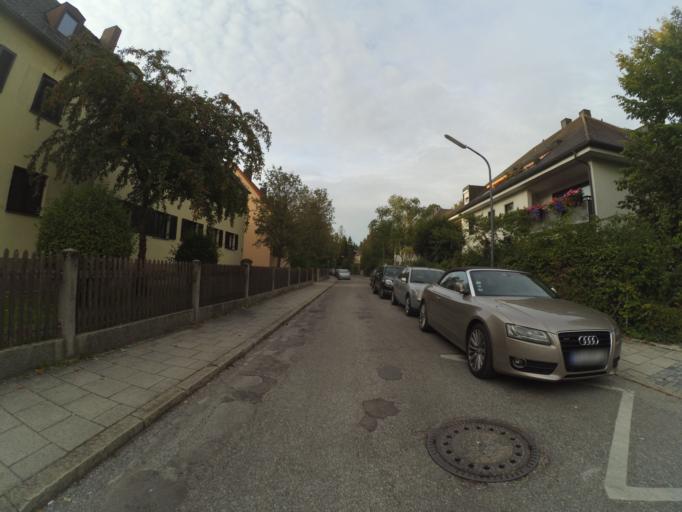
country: DE
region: Bavaria
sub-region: Upper Bavaria
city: Pasing
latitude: 48.1506
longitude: 11.5126
